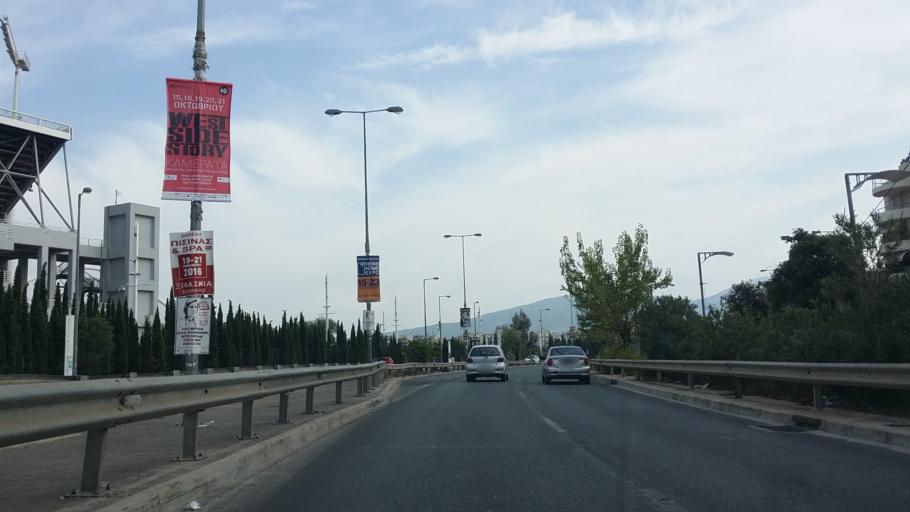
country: GR
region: Attica
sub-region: Nomarchia Athinas
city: Filothei
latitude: 38.0384
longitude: 23.7794
